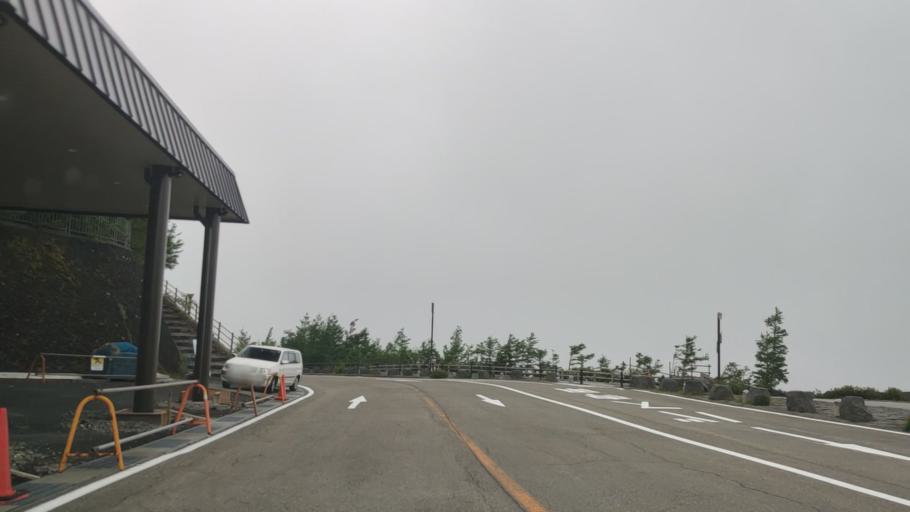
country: JP
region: Yamanashi
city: Fujikawaguchiko
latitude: 35.3941
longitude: 138.7326
